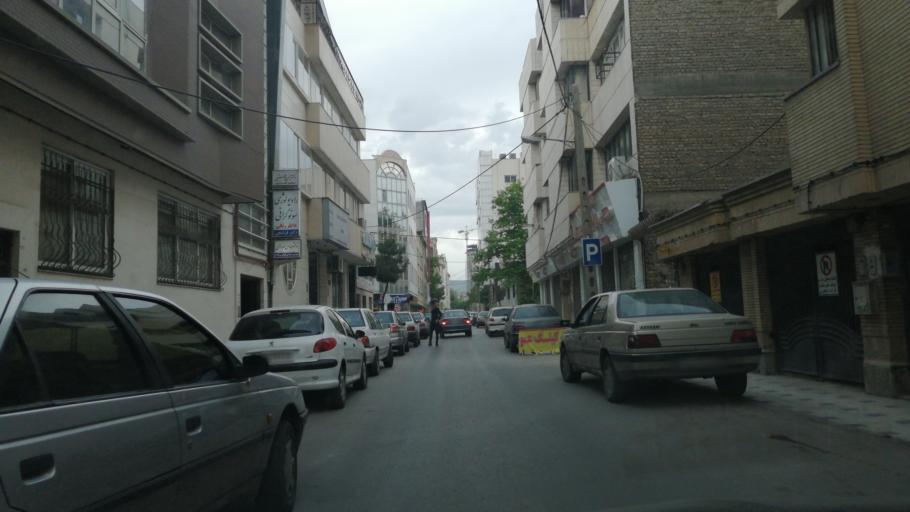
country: IR
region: Razavi Khorasan
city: Mashhad
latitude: 36.2895
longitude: 59.5846
